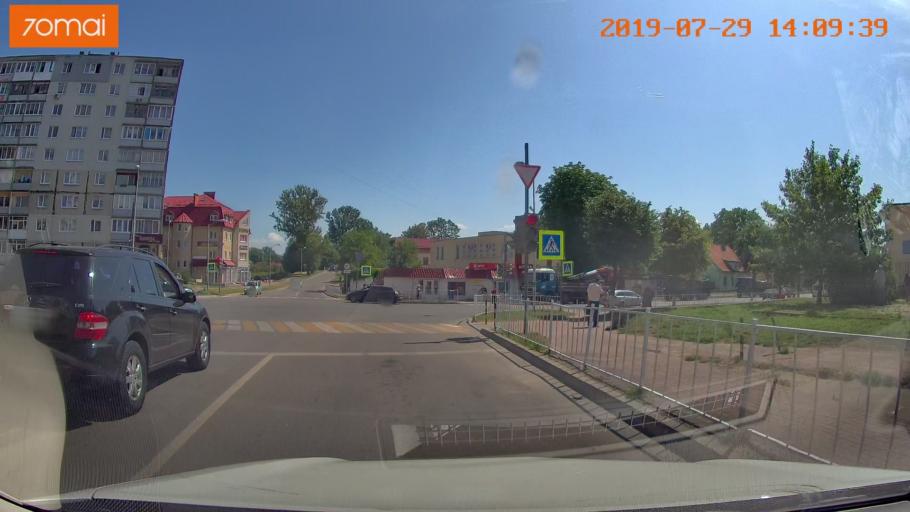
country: RU
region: Kaliningrad
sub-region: Gorod Kaliningrad
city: Baltiysk
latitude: 54.6548
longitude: 19.9113
